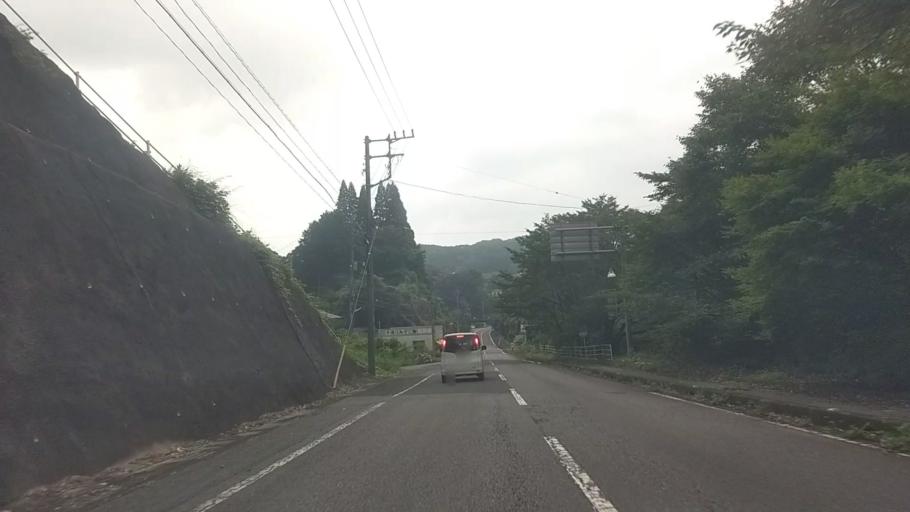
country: JP
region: Chiba
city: Kawaguchi
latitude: 35.2383
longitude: 140.1659
